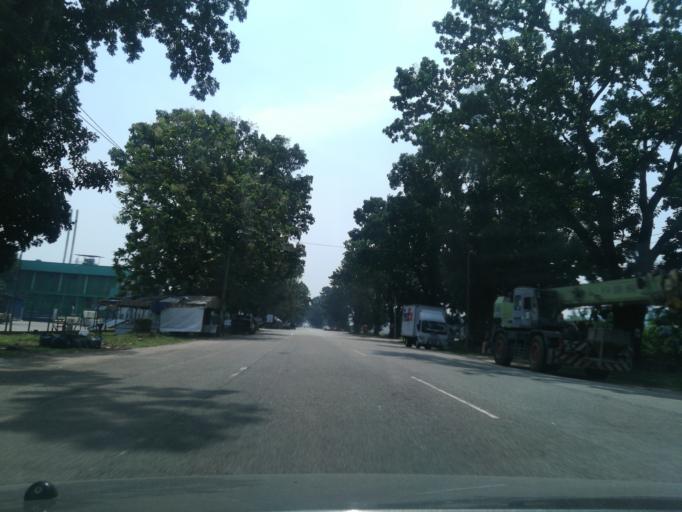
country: MY
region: Kedah
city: Kulim
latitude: 5.4067
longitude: 100.5555
